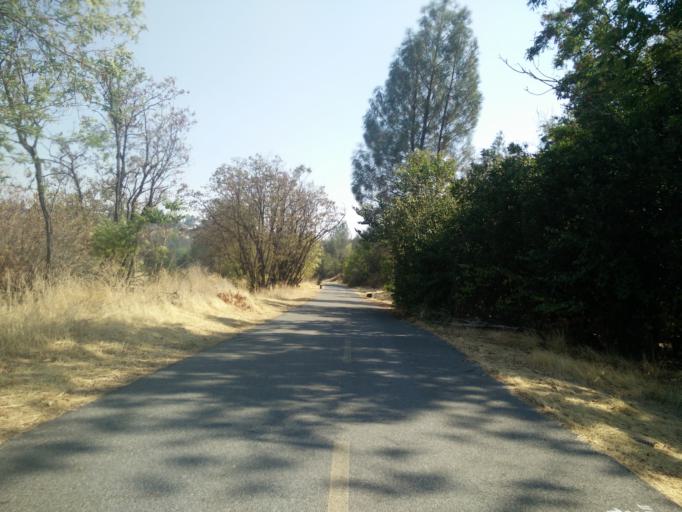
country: US
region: California
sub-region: Shasta County
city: Redding
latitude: 40.5952
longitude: -122.4401
